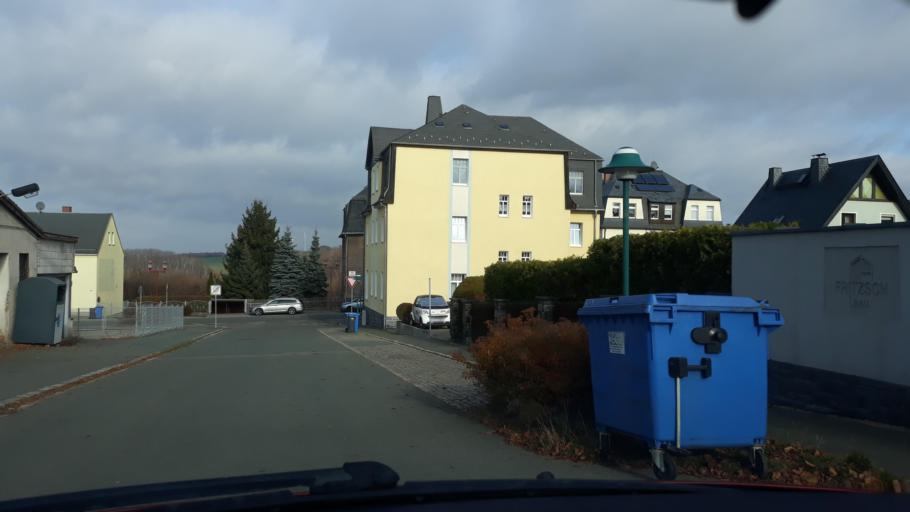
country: DE
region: Saxony
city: Wilkau-Hasslau
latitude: 50.6935
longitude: 12.5378
